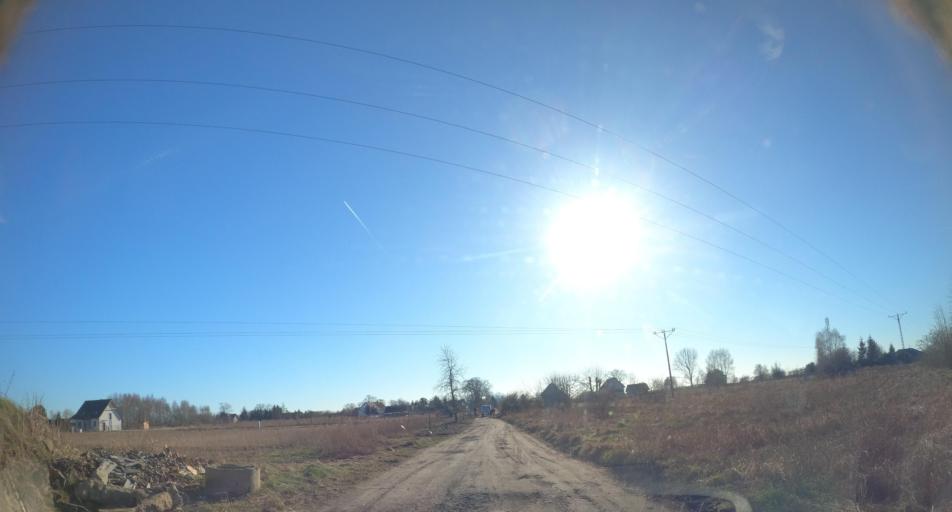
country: PL
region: West Pomeranian Voivodeship
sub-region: Powiat kamienski
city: Dziwnow
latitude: 54.0330
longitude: 14.8362
